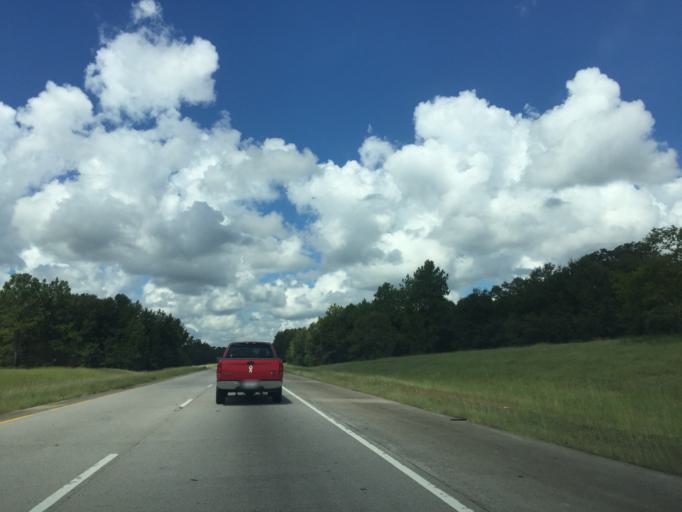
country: US
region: Georgia
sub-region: Candler County
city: Metter
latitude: 32.3801
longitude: -82.2032
